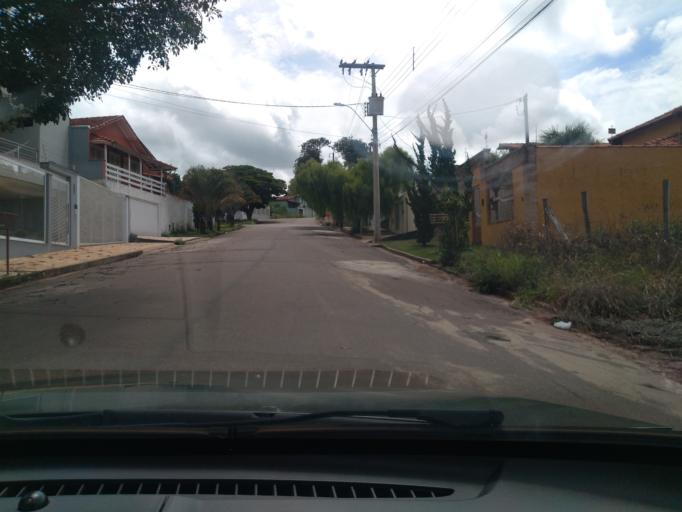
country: BR
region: Minas Gerais
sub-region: Tres Coracoes
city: Tres Coracoes
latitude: -21.6738
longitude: -45.2747
